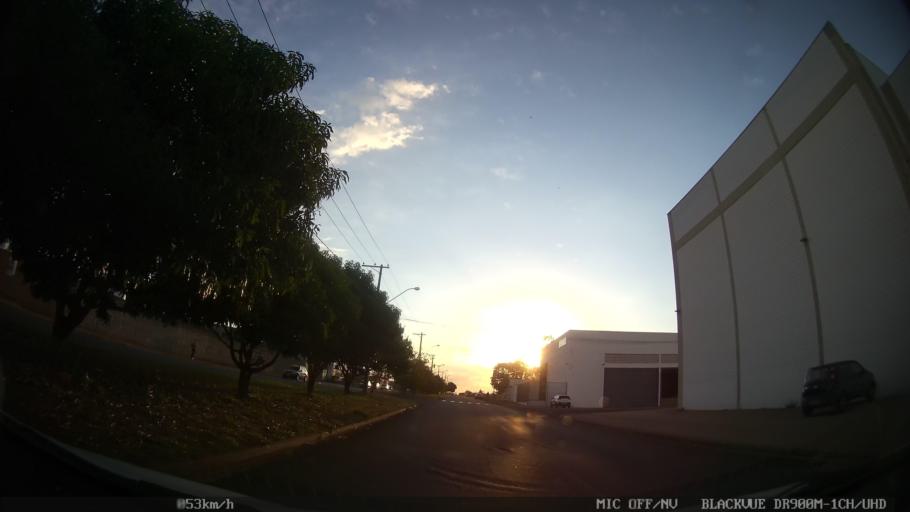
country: BR
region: Sao Paulo
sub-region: Ribeirao Preto
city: Ribeirao Preto
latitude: -21.1524
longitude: -47.7599
